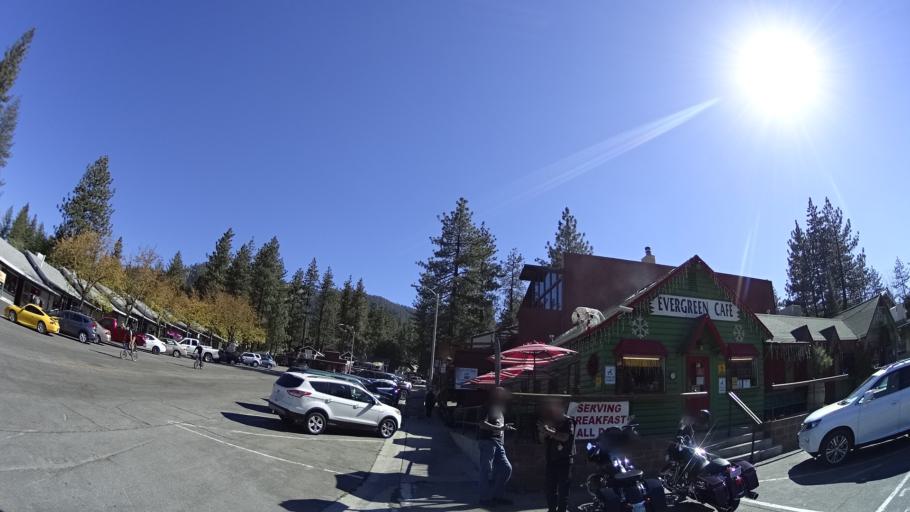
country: US
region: California
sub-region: San Bernardino County
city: Wrightwood
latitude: 34.3602
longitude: -117.6338
